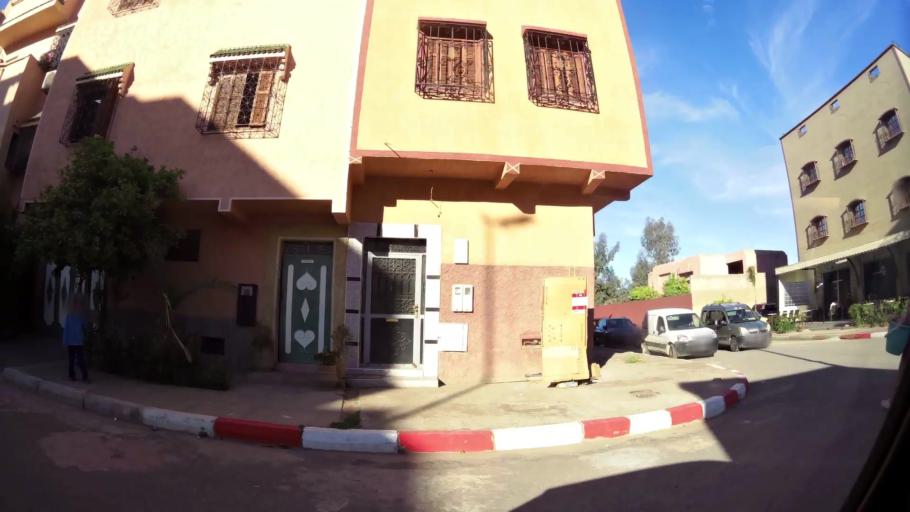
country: MA
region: Marrakech-Tensift-Al Haouz
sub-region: Marrakech
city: Marrakesh
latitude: 31.6182
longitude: -8.0695
